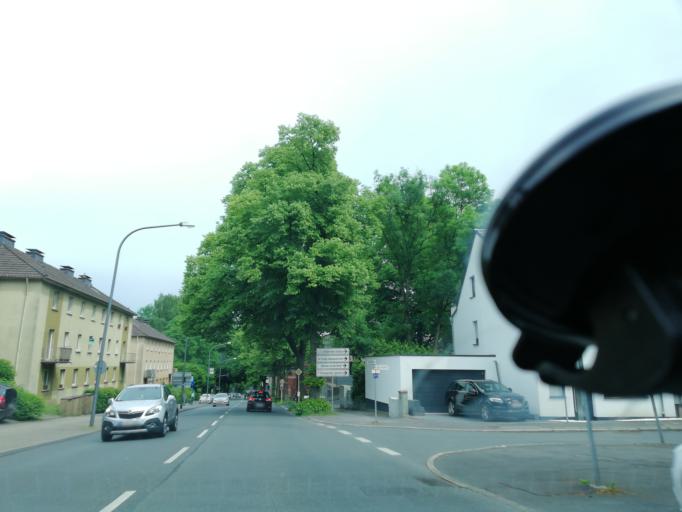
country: DE
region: North Rhine-Westphalia
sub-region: Regierungsbezirk Dusseldorf
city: Wuppertal
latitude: 51.2683
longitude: 7.1723
